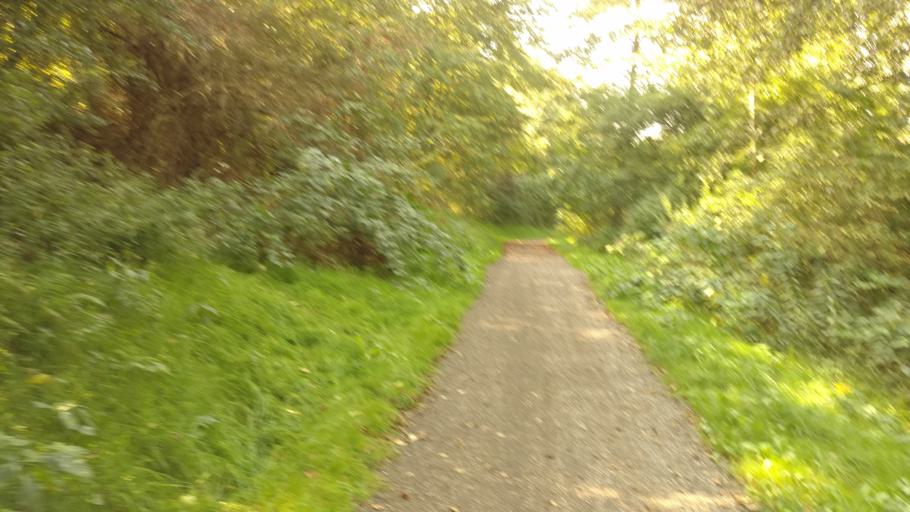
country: PL
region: Lesser Poland Voivodeship
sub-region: Powiat krakowski
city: Michalowice
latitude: 50.1302
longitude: 19.9785
